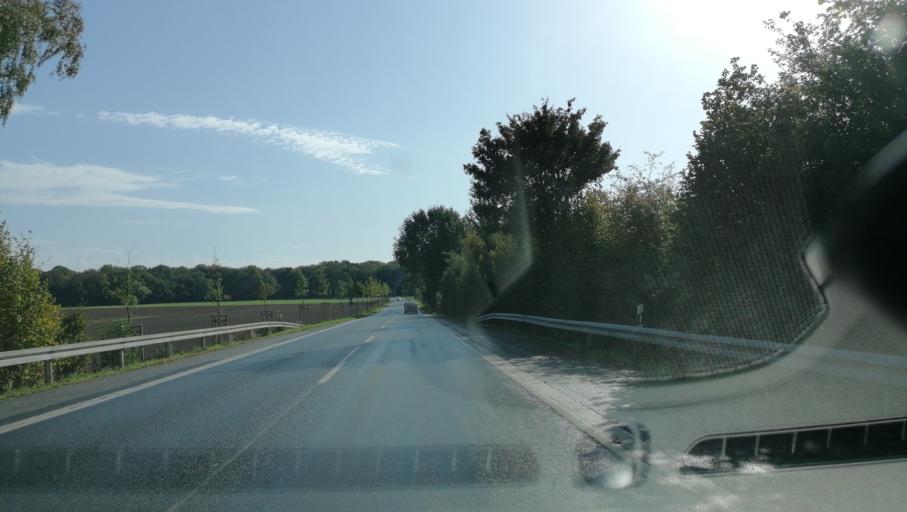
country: DE
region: North Rhine-Westphalia
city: Datteln
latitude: 51.6302
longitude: 7.3498
